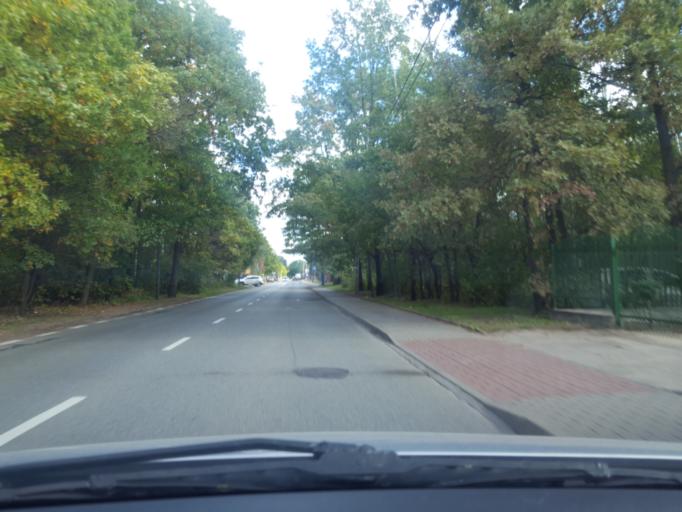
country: PL
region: Masovian Voivodeship
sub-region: Warszawa
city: Rembertow
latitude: 52.2723
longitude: 21.1554
